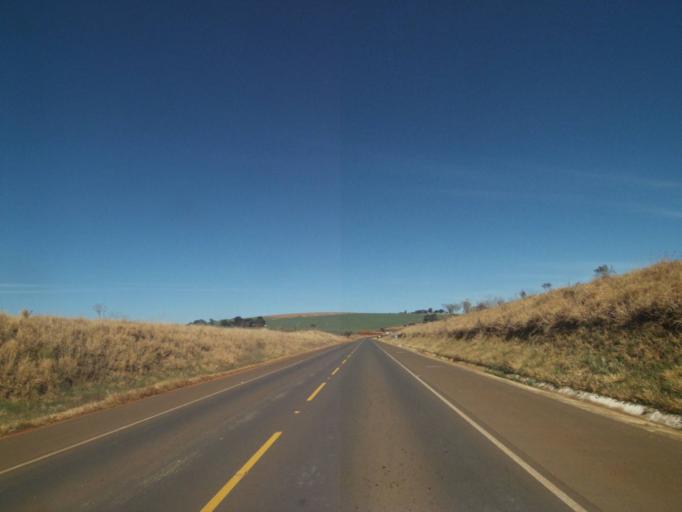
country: BR
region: Parana
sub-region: Tibagi
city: Tibagi
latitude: -24.7427
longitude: -50.4601
